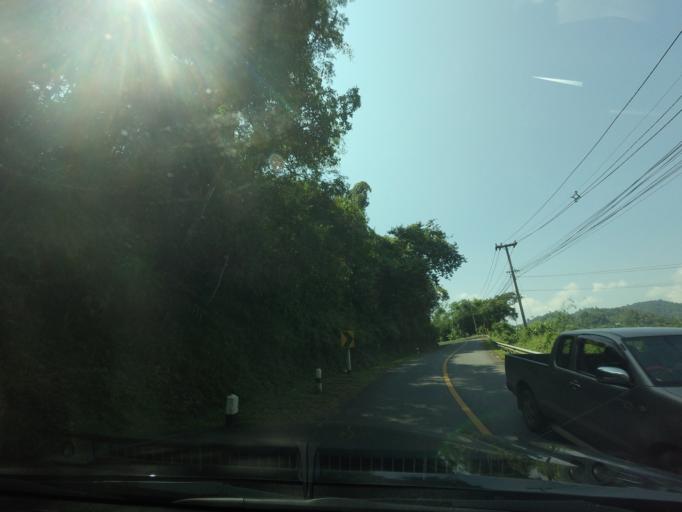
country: TH
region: Nan
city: Bo Kluea
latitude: 19.0863
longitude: 101.1537
